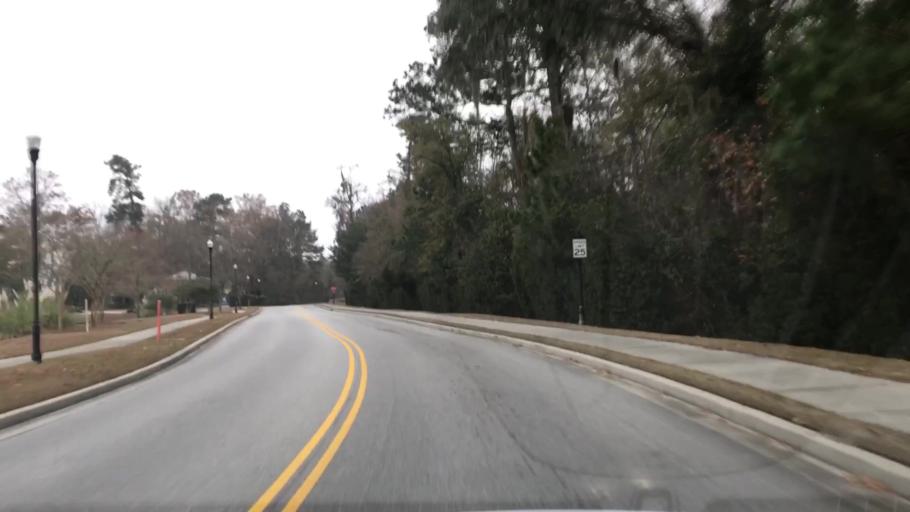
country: US
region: South Carolina
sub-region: Charleston County
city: Shell Point
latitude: 32.8032
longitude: -80.0805
